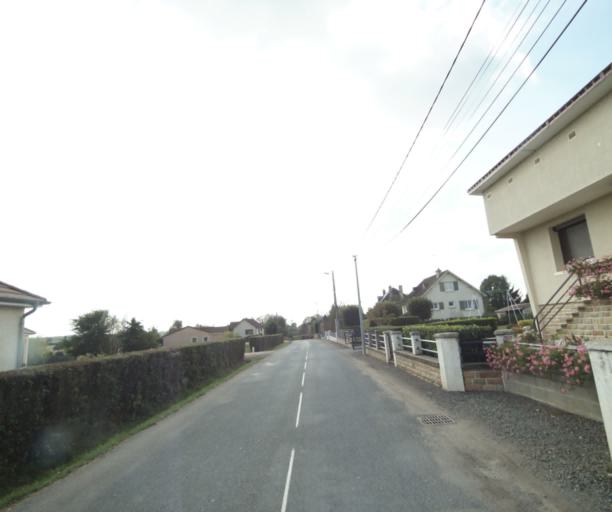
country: FR
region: Bourgogne
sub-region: Departement de Saone-et-Loire
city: Palinges
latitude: 46.4956
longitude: 4.2170
